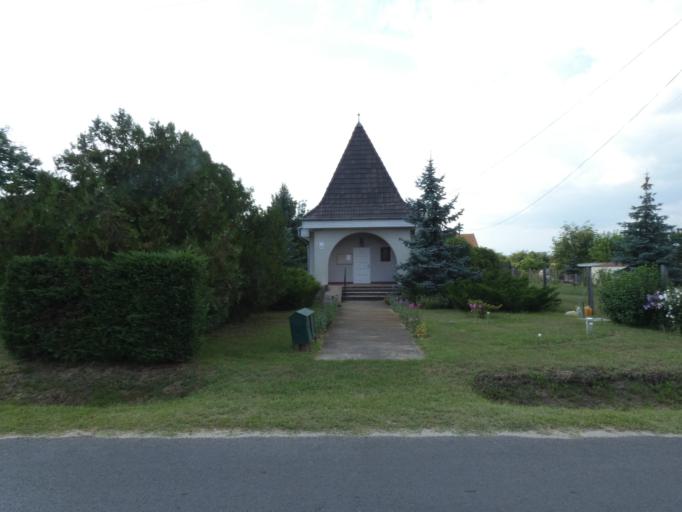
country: HU
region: Pest
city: Taborfalva
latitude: 47.1058
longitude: 19.4862
